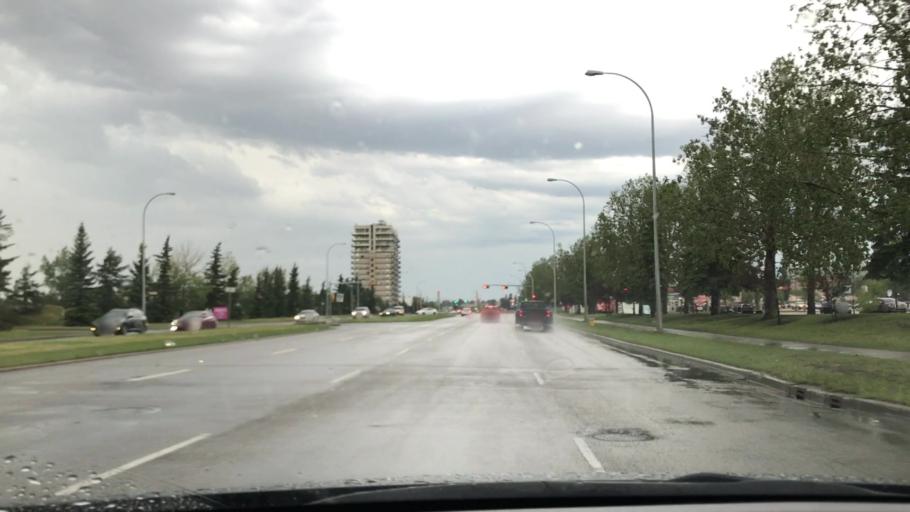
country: CA
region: Alberta
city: Edmonton
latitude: 53.4547
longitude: -113.4345
